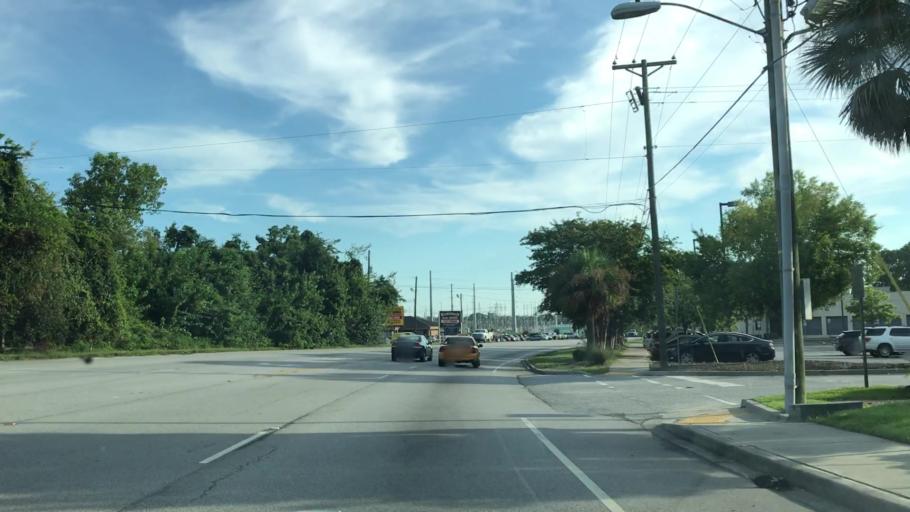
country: US
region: South Carolina
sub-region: Charleston County
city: North Charleston
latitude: 32.8455
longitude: -80.0151
